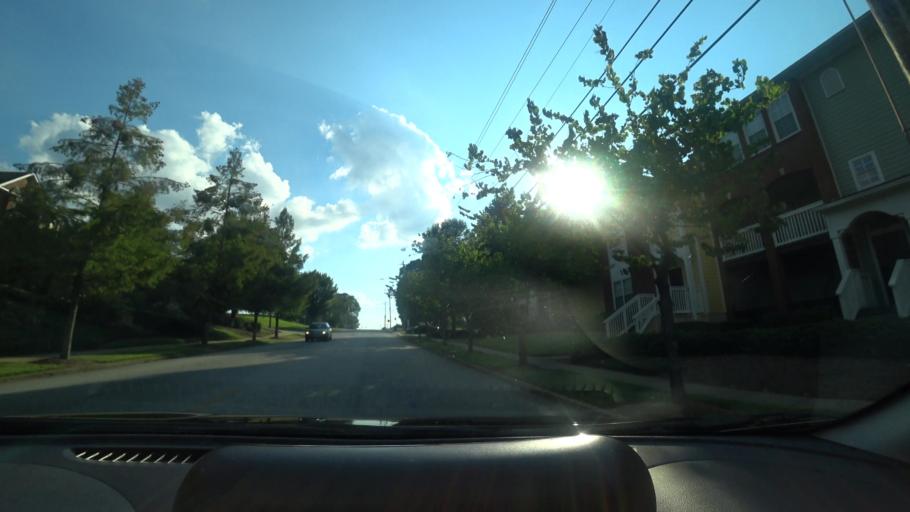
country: US
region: Georgia
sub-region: Fulton County
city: Atlanta
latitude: 33.7080
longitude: -84.3954
